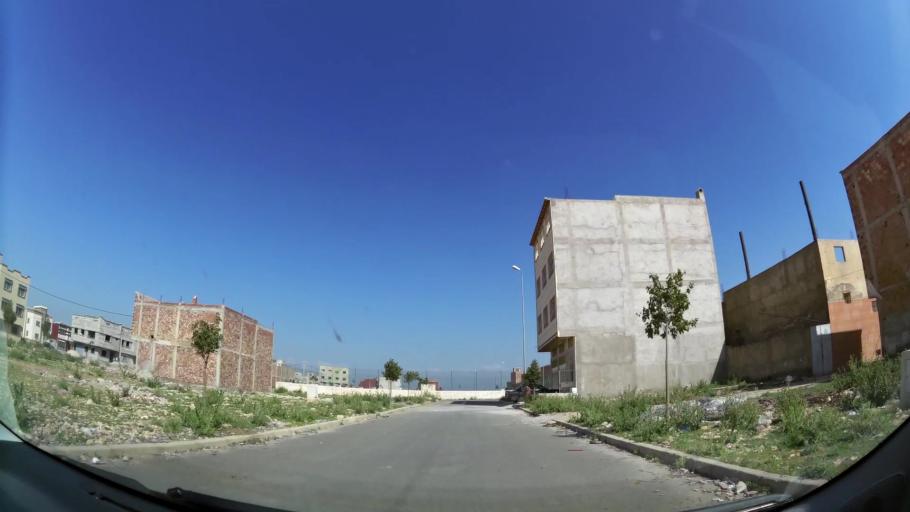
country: MA
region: Oriental
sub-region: Oujda-Angad
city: Oujda
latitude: 34.6959
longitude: -1.8720
